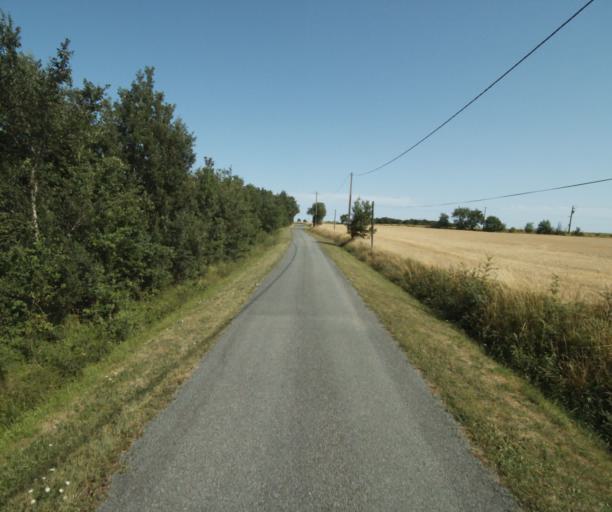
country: FR
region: Midi-Pyrenees
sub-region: Departement de la Haute-Garonne
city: Saint-Felix-Lauragais
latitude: 43.4268
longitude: 1.8400
